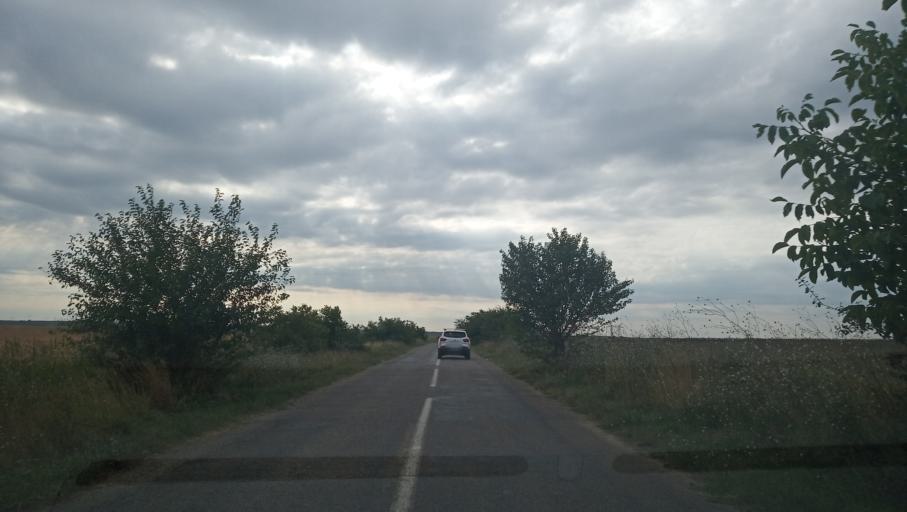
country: RO
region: Constanta
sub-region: Comuna Adamclisi
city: Adamclisi
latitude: 44.0280
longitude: 27.9835
